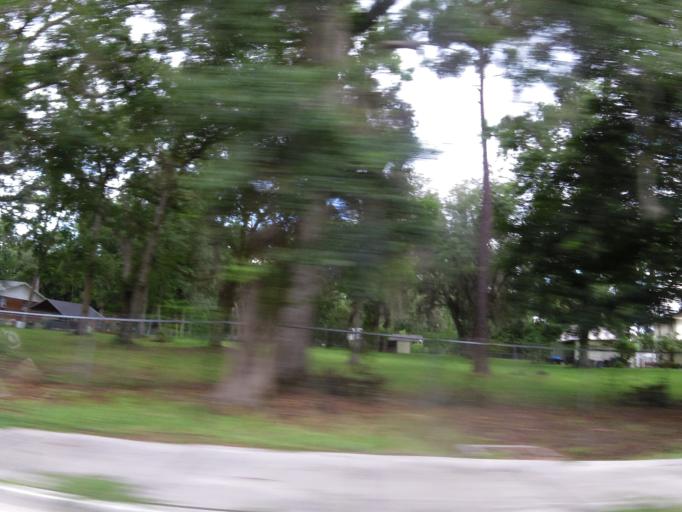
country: US
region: Florida
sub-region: Duval County
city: Jacksonville
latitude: 30.4209
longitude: -81.6913
